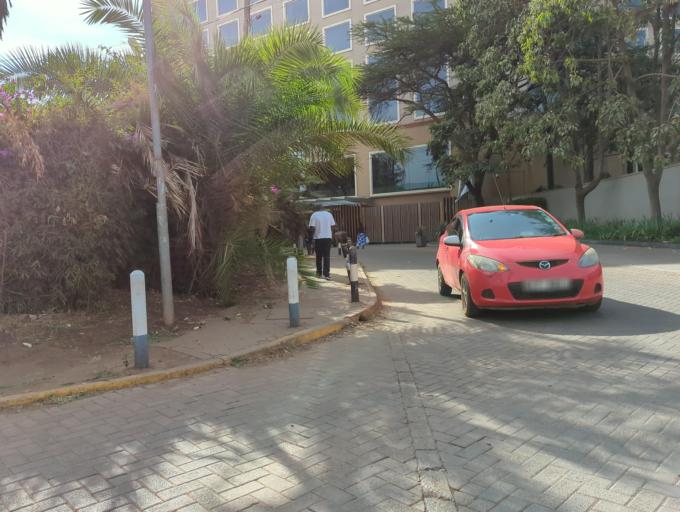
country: KE
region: Nairobi Area
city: Nairobi
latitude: -1.2628
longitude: 36.8028
